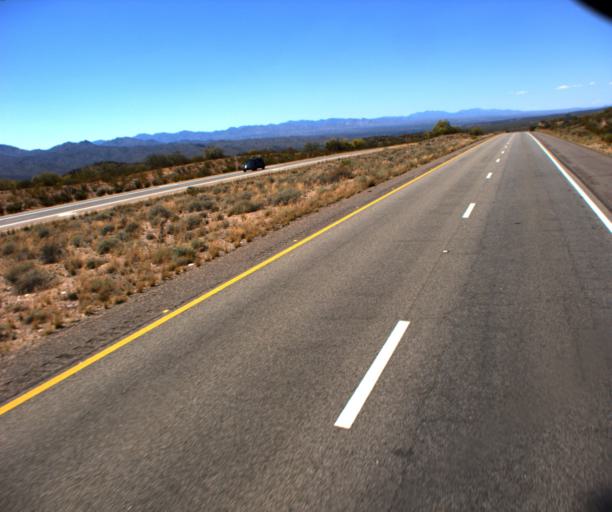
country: US
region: Arizona
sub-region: Yavapai County
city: Bagdad
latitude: 34.6099
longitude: -113.5242
